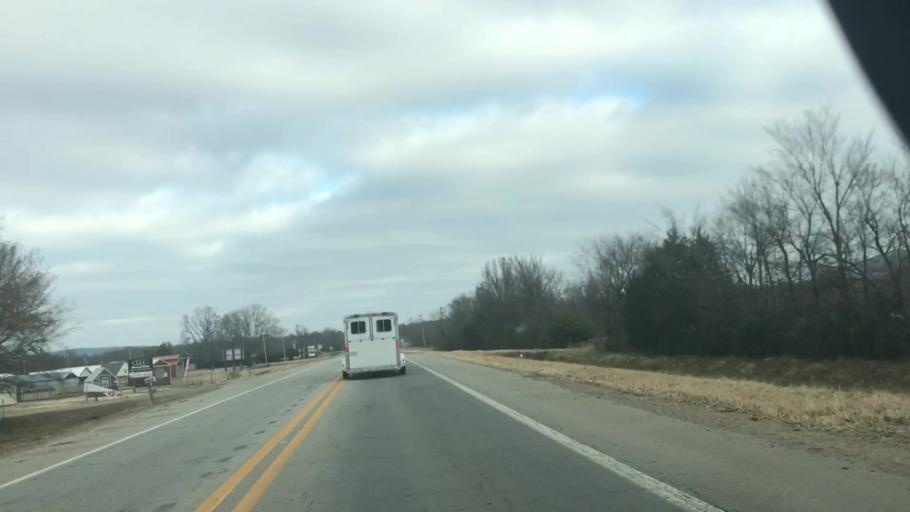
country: US
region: Arkansas
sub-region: Scott County
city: Waldron
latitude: 34.9056
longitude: -94.1073
